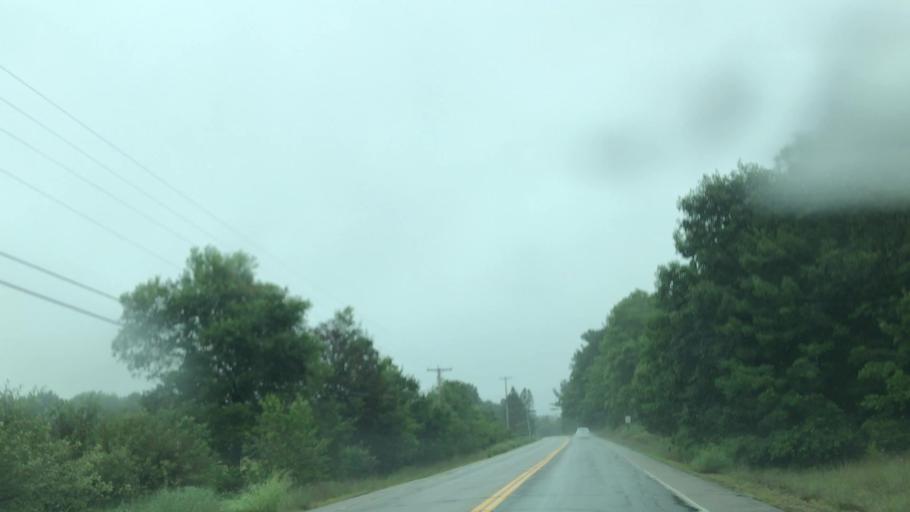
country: US
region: Maine
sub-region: York County
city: North Berwick
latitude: 43.2994
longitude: -70.7620
